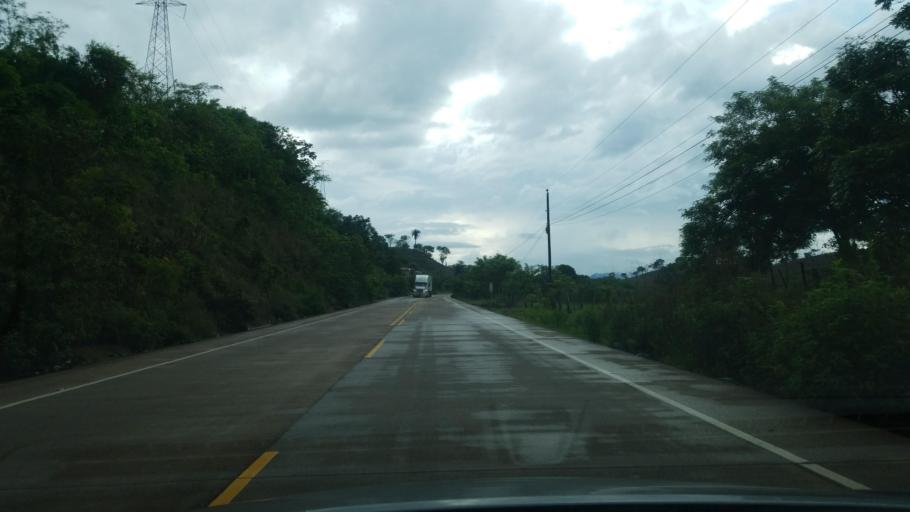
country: HN
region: Copan
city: Copan
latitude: 14.8560
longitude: -89.2041
